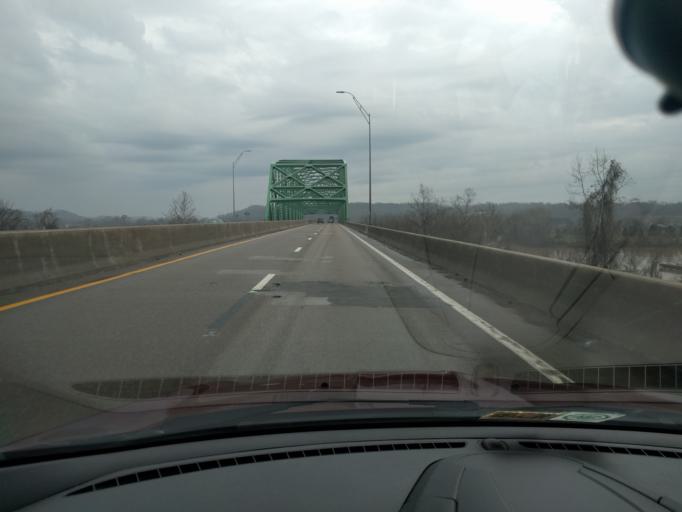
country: US
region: West Virginia
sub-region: Wood County
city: Williamstown
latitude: 39.4029
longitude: -81.4310
